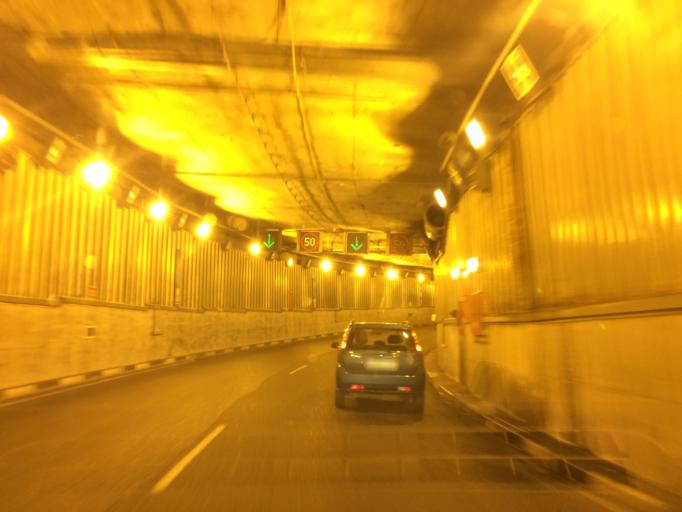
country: ES
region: Madrid
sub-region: Provincia de Madrid
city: Pinar de Chamartin
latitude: 40.4728
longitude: -3.6754
